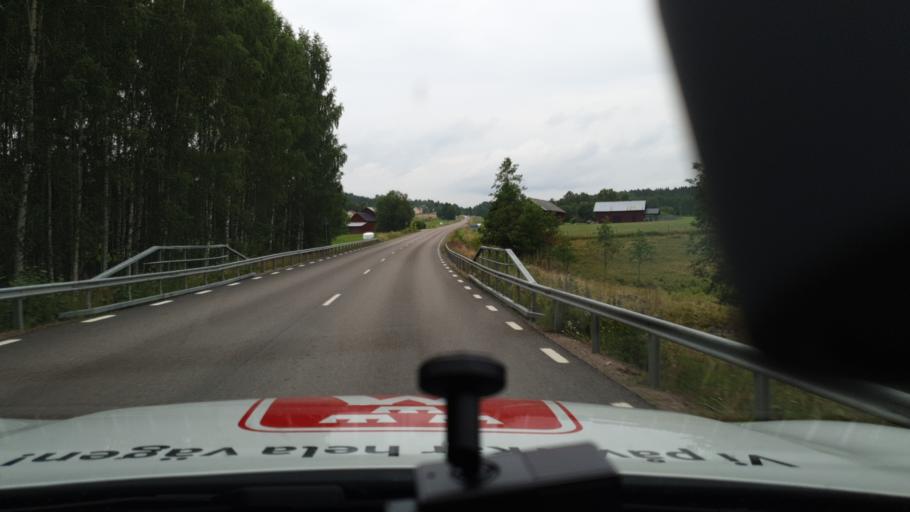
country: SE
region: Vaermland
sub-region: Torsby Kommun
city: Torsby
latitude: 60.0249
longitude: 13.1341
